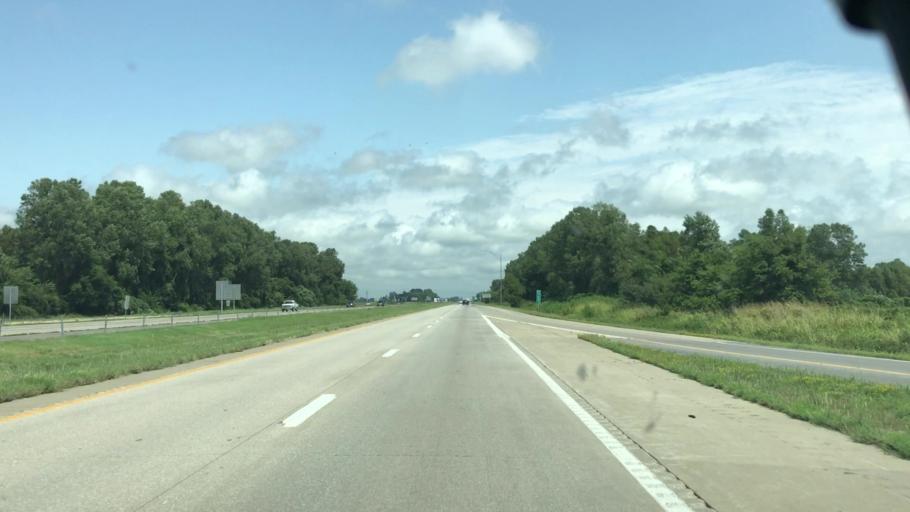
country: US
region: Missouri
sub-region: Pemiscot County
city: Steele
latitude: 36.0916
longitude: -89.7934
